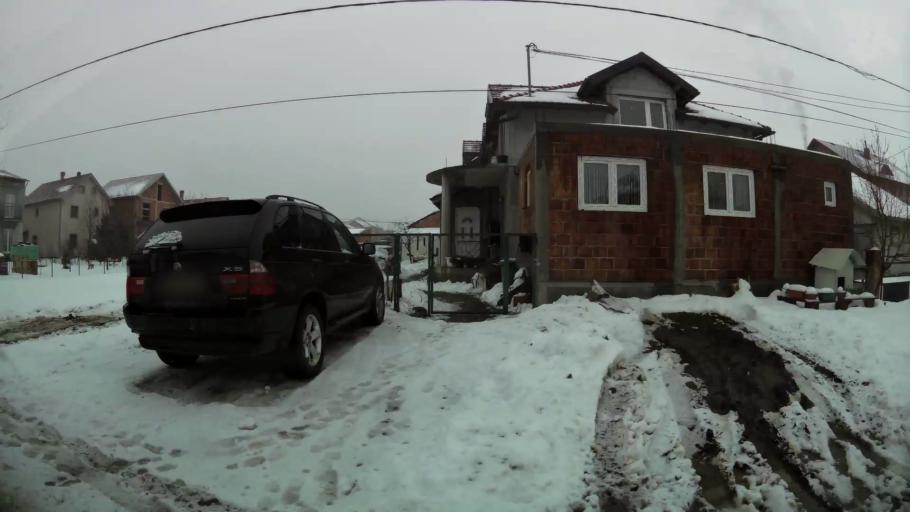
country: RS
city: Novi Banovci
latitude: 44.8759
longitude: 20.3115
